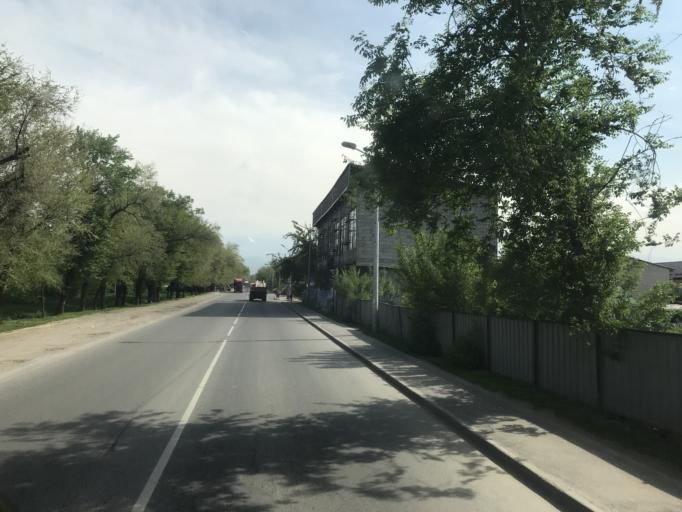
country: KZ
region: Almaty Qalasy
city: Almaty
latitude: 43.2456
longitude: 76.8043
